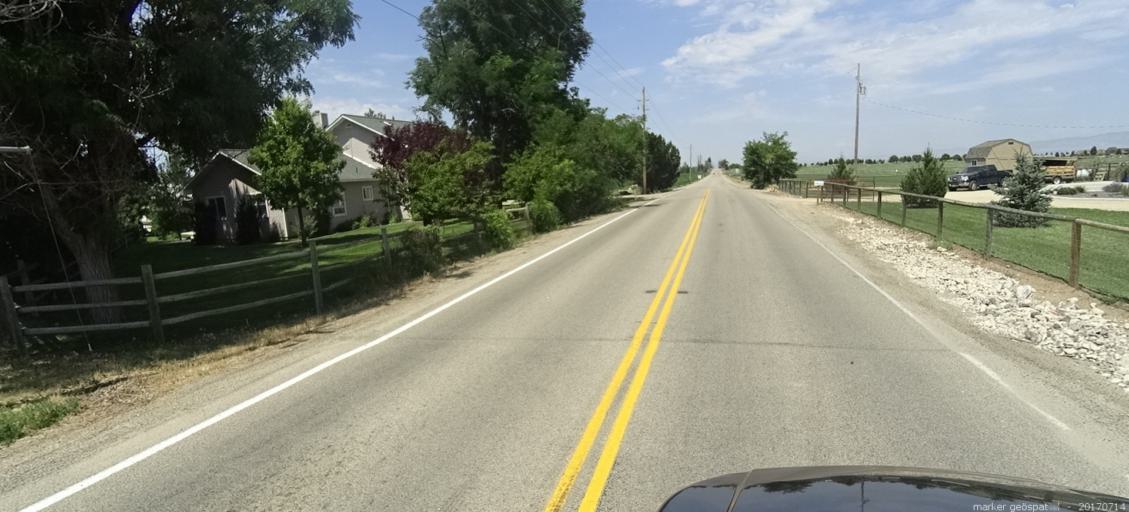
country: US
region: Idaho
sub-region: Ada County
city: Kuna
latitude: 43.5323
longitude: -116.3543
